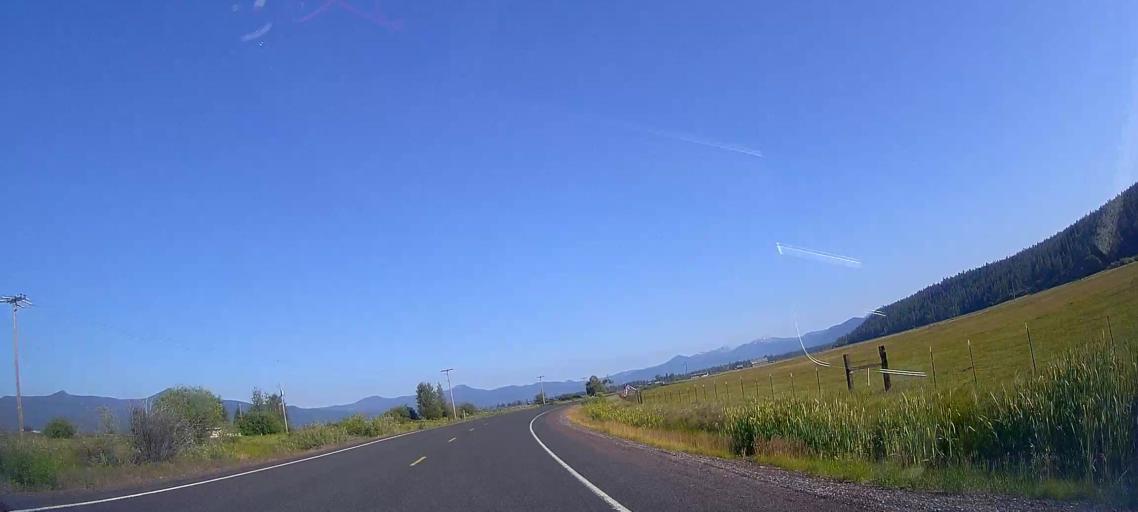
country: US
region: Oregon
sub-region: Klamath County
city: Klamath Falls
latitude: 42.6472
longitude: -121.9534
